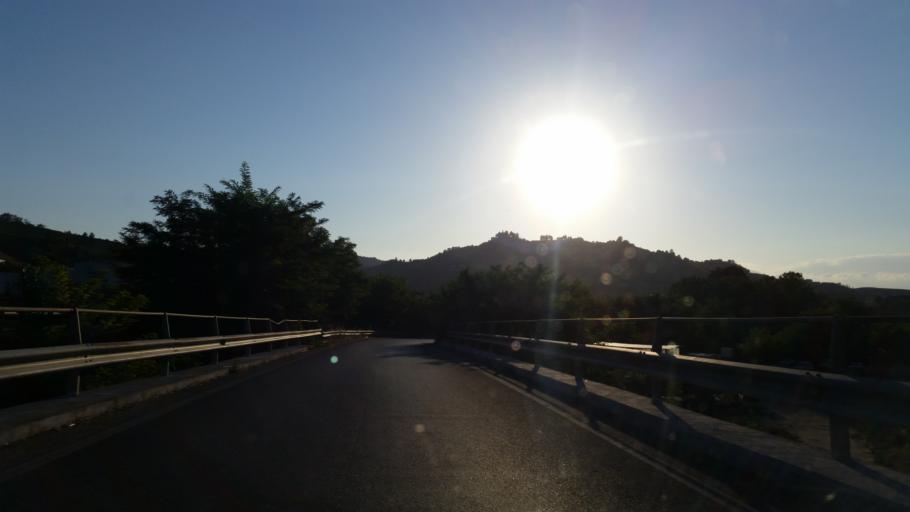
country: IT
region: Piedmont
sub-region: Provincia di Cuneo
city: Santo Stefano Belbo
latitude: 44.7118
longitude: 8.2490
